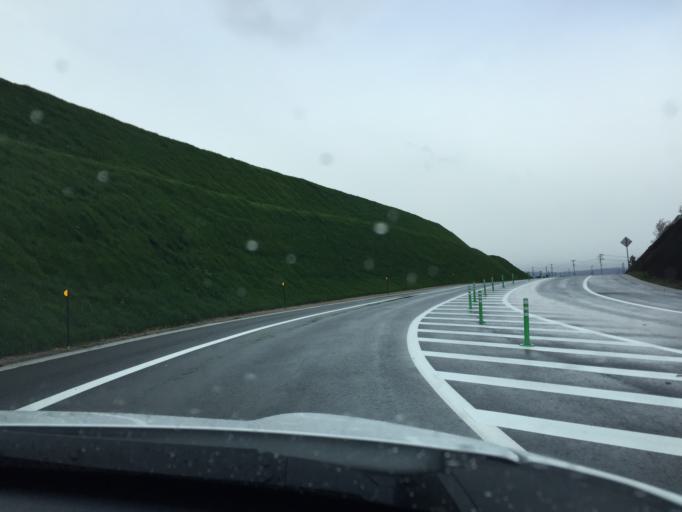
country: JP
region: Yamagata
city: Yonezawa
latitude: 37.8944
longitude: 140.1620
